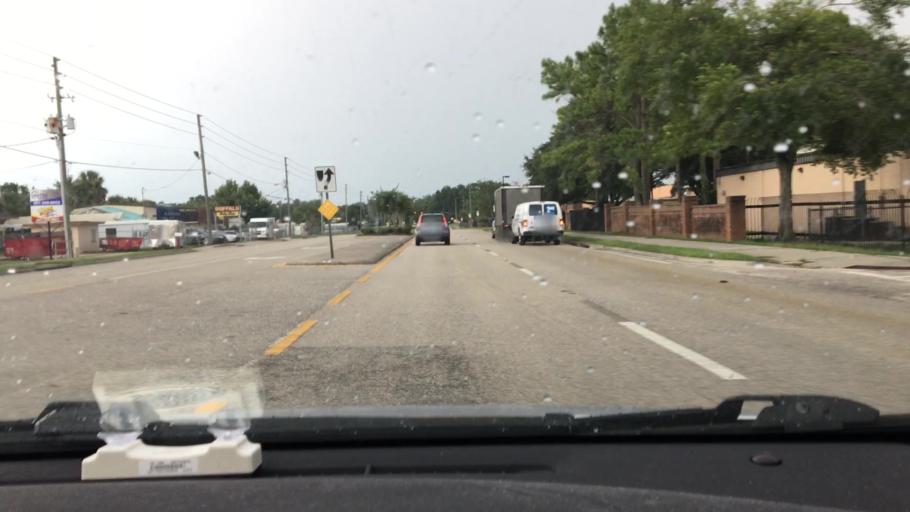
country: US
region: Florida
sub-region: Seminole County
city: Casselberry
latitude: 28.6799
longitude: -81.3478
